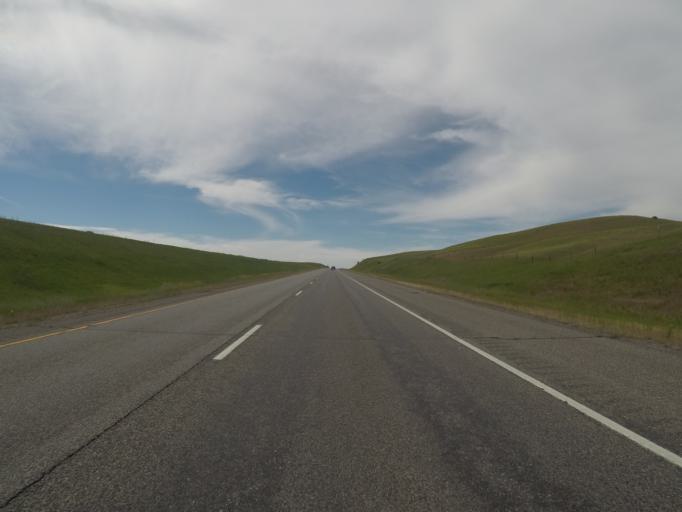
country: US
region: Montana
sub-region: Stillwater County
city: Columbus
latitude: 45.6130
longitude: -109.1734
